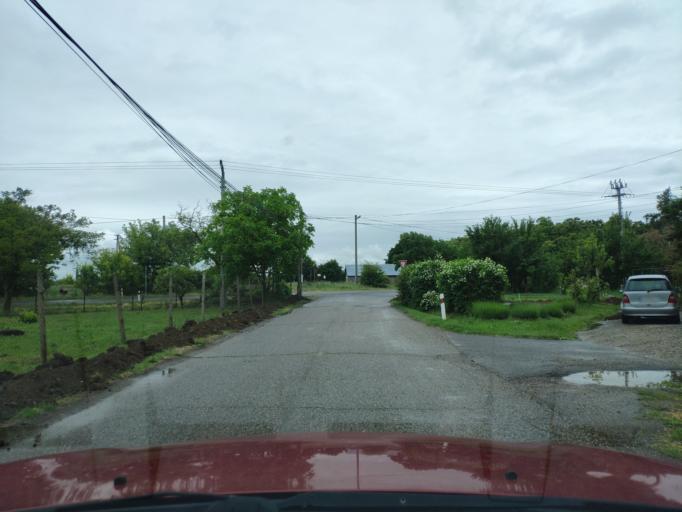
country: HU
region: Borsod-Abauj-Zemplen
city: Karcsa
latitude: 48.3976
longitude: 21.8076
